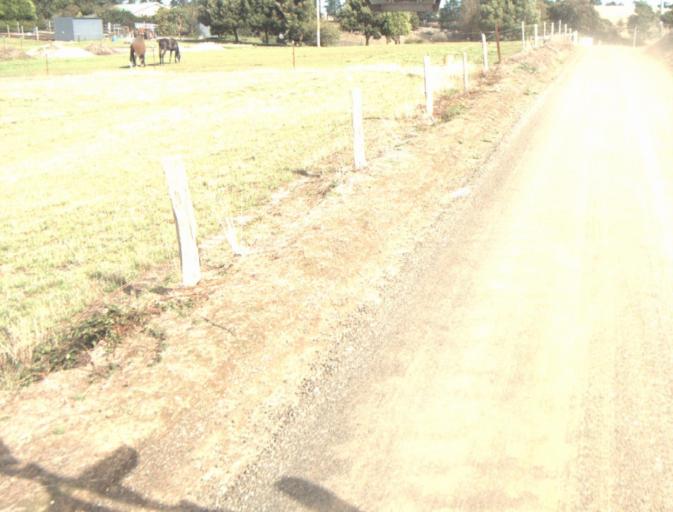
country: AU
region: Tasmania
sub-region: Launceston
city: Mayfield
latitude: -41.1893
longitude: 147.1907
